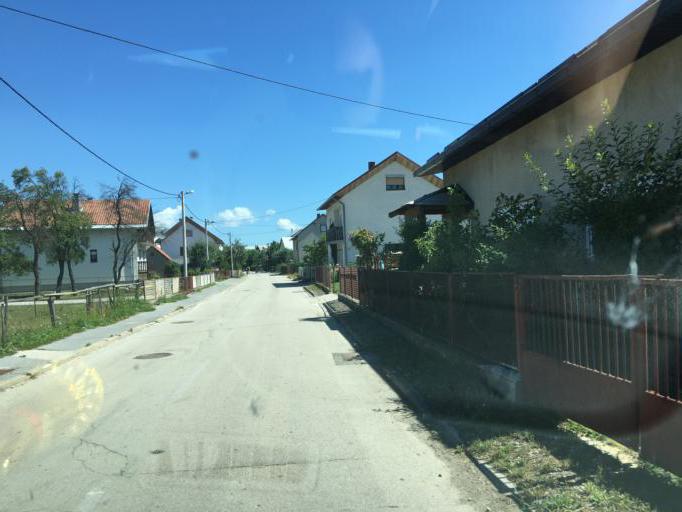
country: HR
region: Licko-Senjska
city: Gospic
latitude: 44.5506
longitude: 15.3599
